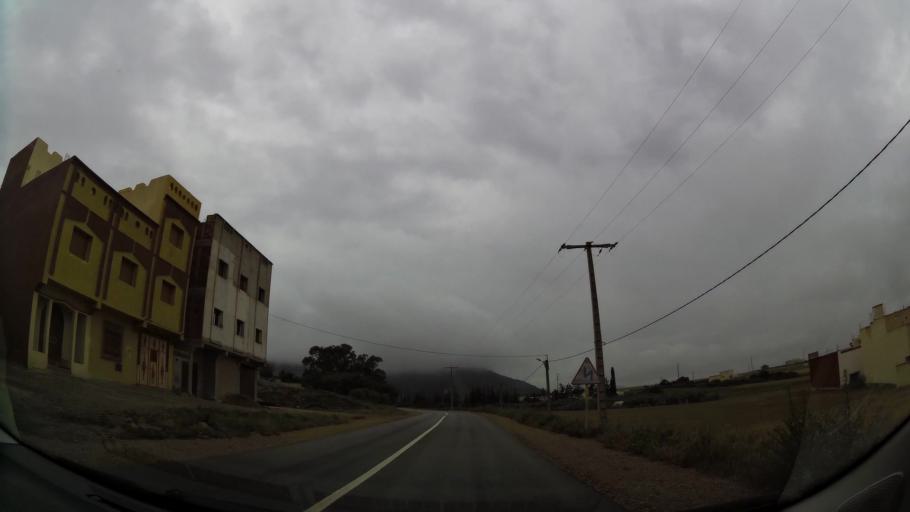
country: MA
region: Oriental
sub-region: Nador
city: Nador
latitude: 35.1394
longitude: -3.0494
